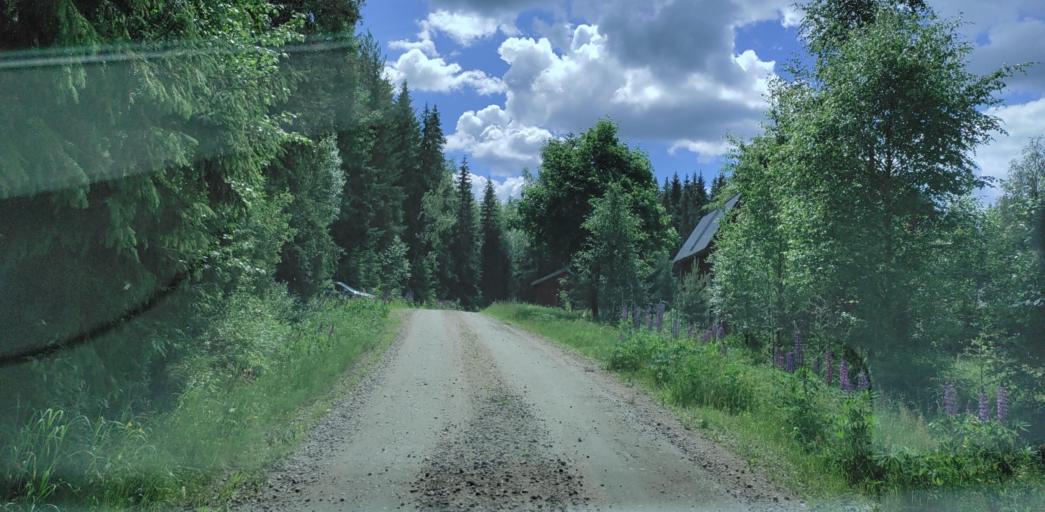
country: SE
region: Vaermland
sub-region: Hagfors Kommun
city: Ekshaerad
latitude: 60.0758
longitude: 13.3131
